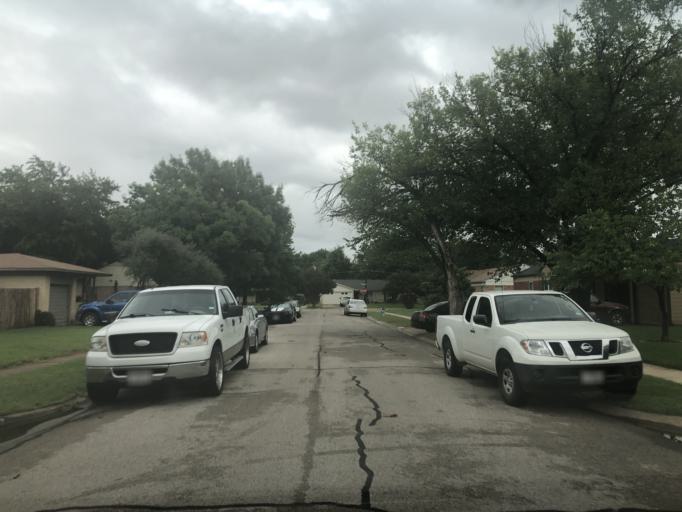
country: US
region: Texas
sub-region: Dallas County
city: Irving
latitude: 32.7991
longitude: -96.9505
